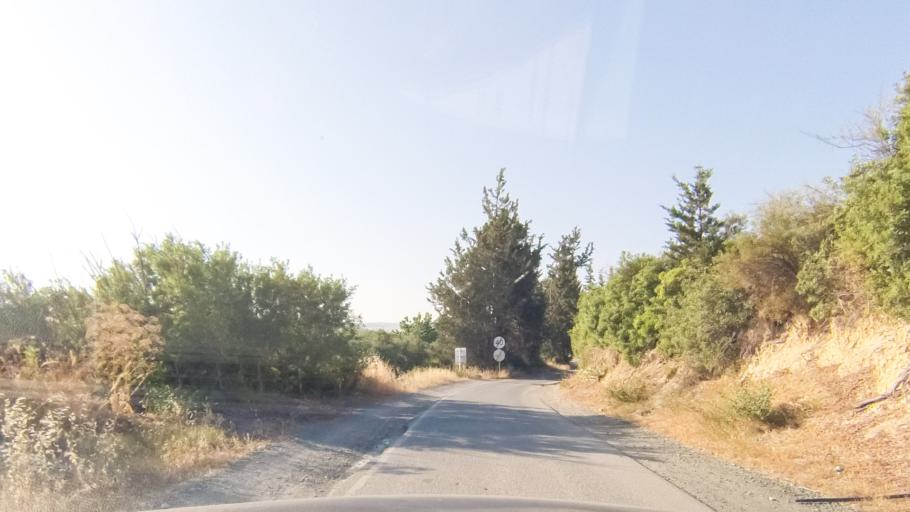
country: CY
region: Limassol
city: Pissouri
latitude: 34.6758
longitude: 32.7606
